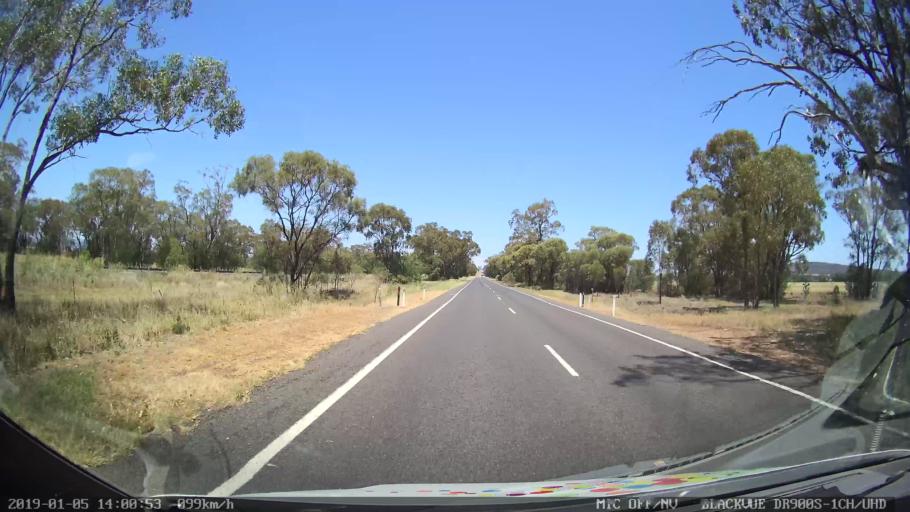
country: AU
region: New South Wales
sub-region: Gunnedah
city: Gunnedah
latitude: -31.1642
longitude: 150.3181
